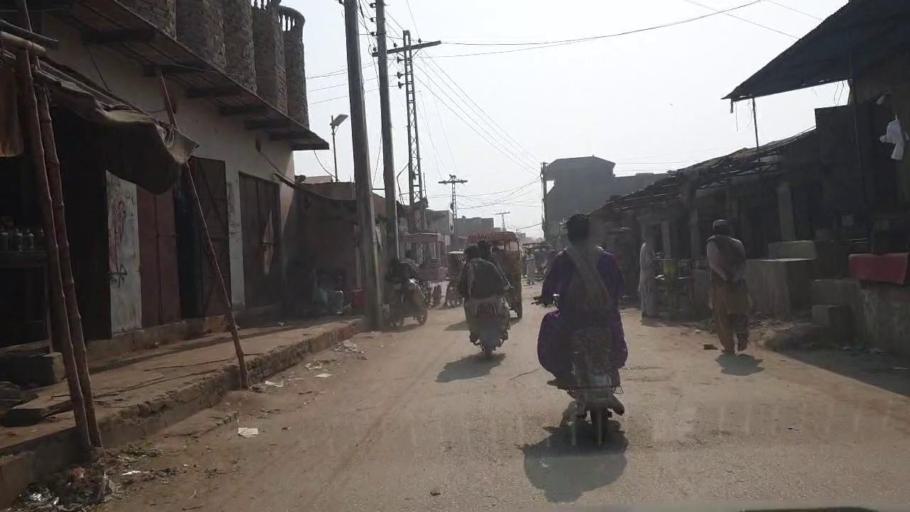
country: PK
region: Sindh
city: Bhit Shah
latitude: 25.8078
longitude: 68.4881
